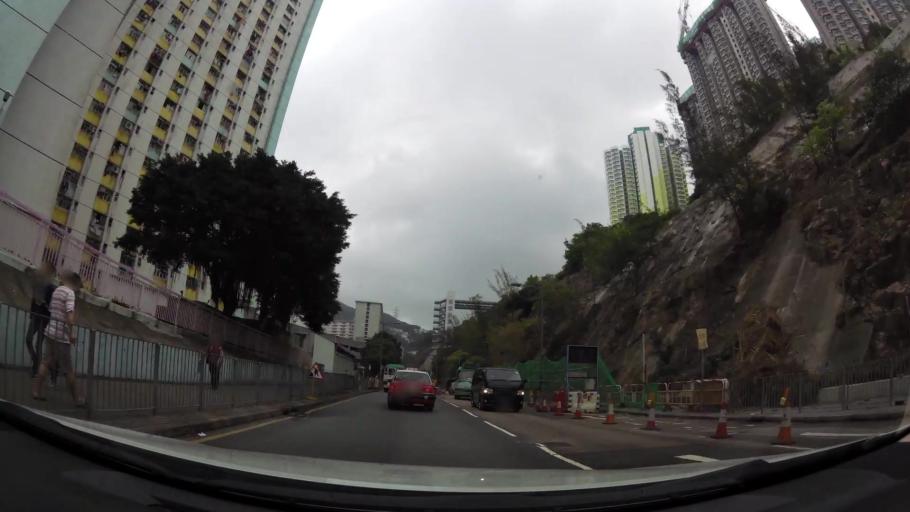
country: HK
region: Kowloon City
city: Kowloon
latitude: 22.3274
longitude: 114.2267
